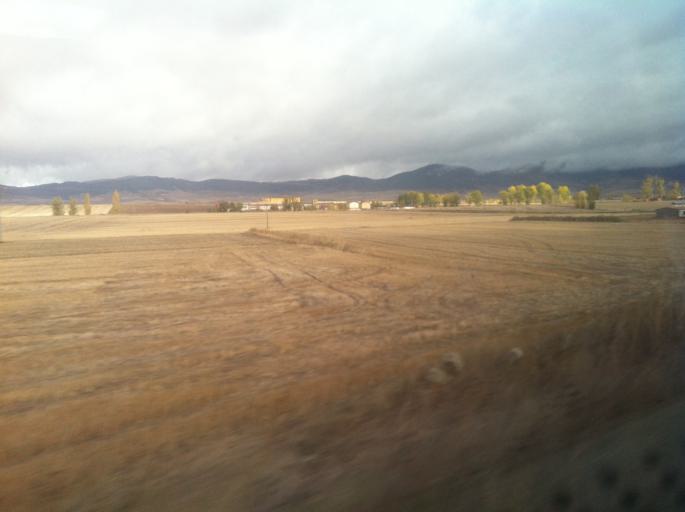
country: ES
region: Castille and Leon
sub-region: Provincia de Burgos
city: Berzosa de Bureba
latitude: 42.6219
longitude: -3.2503
